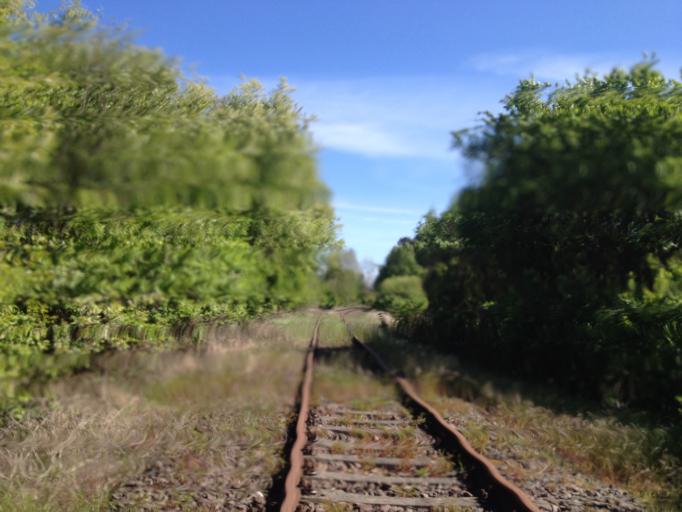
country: DE
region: Brandenburg
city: Templin
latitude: 53.1398
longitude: 13.4237
